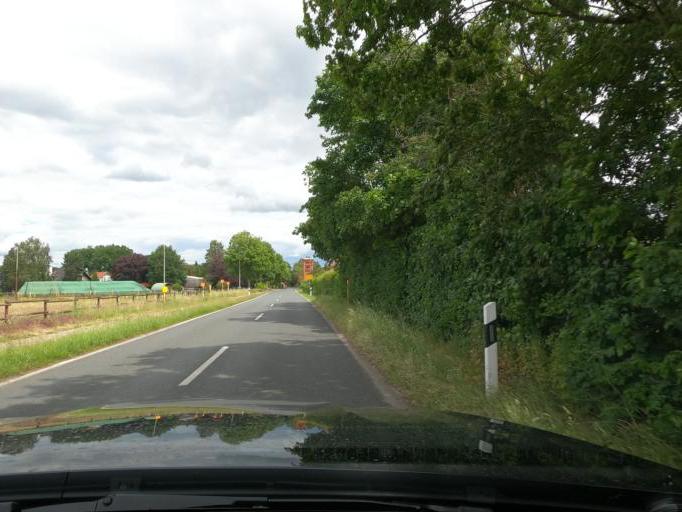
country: DE
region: Lower Saxony
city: Lehrte
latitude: 52.4183
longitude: 9.9497
